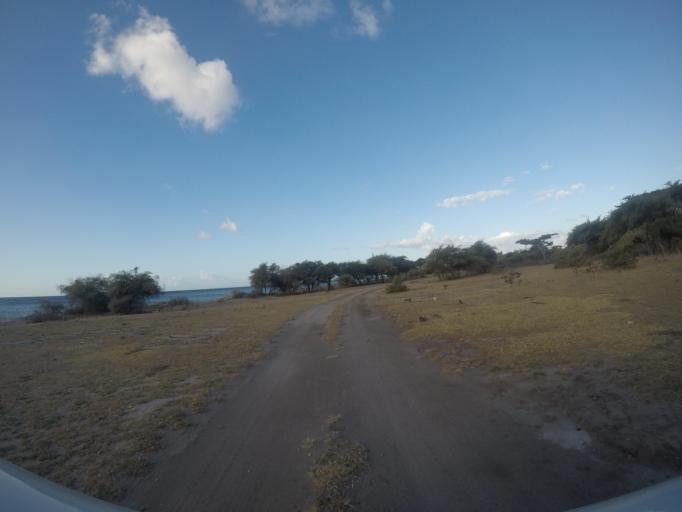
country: TL
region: Lautem
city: Lospalos
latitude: -8.3239
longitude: 126.9947
